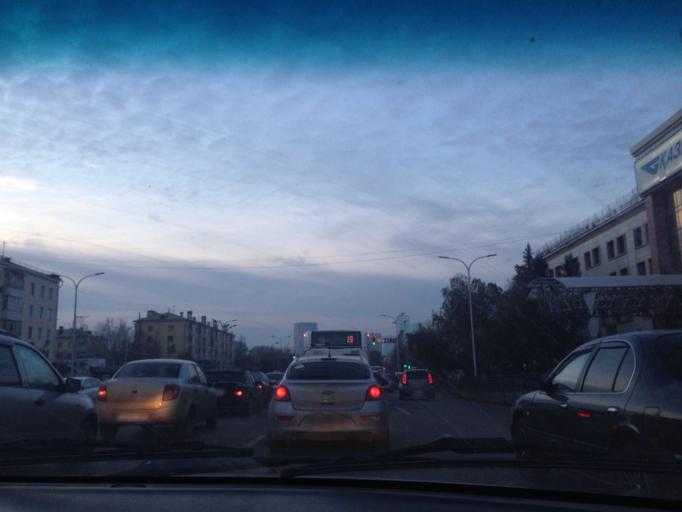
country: KZ
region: Astana Qalasy
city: Astana
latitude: 51.1776
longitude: 71.4181
